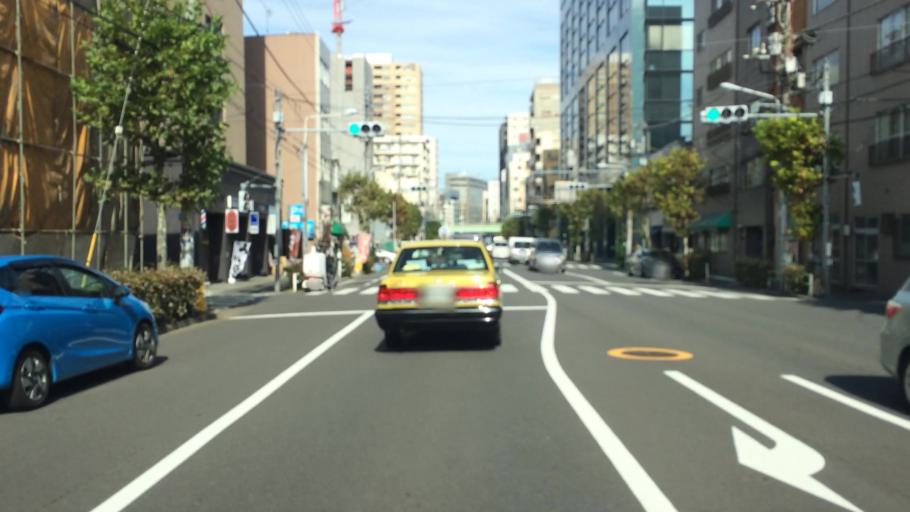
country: JP
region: Tokyo
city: Tokyo
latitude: 35.7117
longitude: 139.7831
